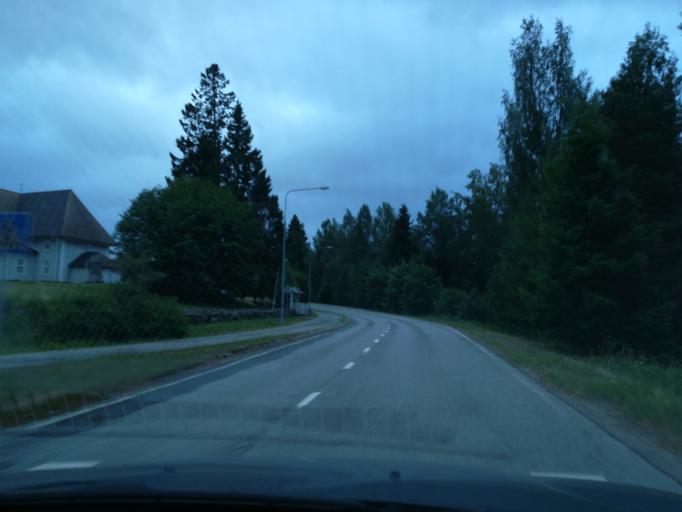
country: FI
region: Southern Savonia
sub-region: Mikkeli
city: Ristiina
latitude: 61.5016
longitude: 27.2654
